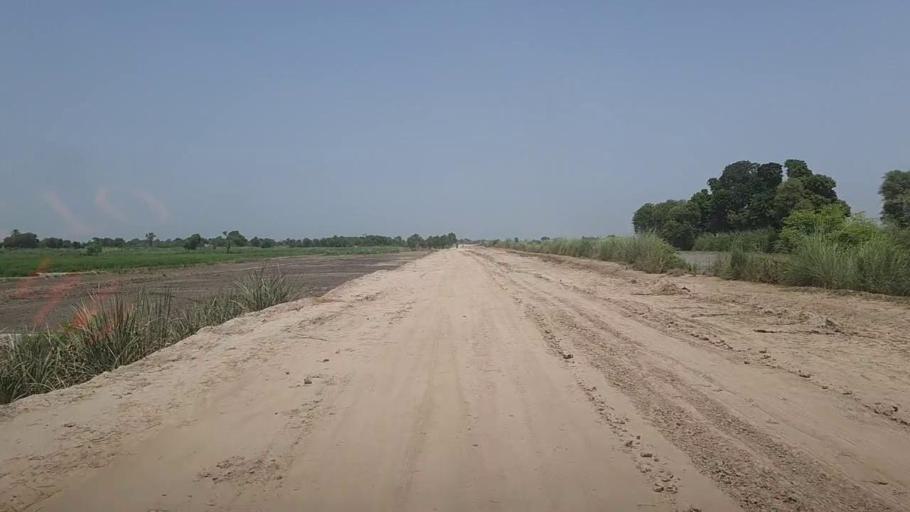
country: PK
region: Sindh
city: Pad Idan
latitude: 26.8022
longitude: 68.2727
